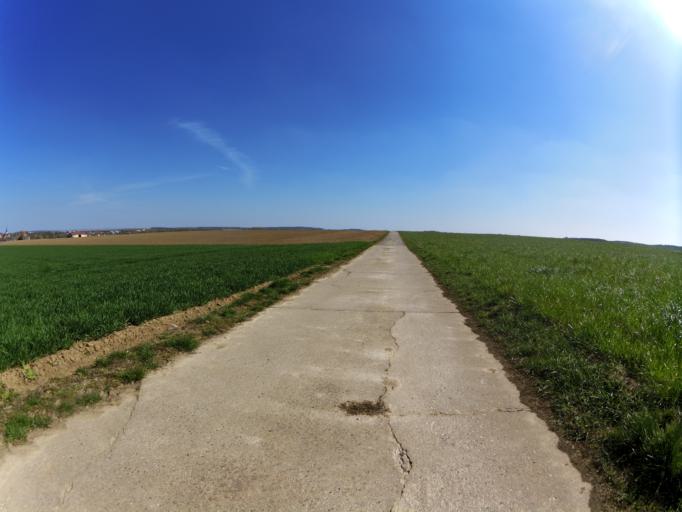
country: DE
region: Bavaria
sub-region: Regierungsbezirk Unterfranken
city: Kurnach
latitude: 49.8725
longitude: 10.0154
